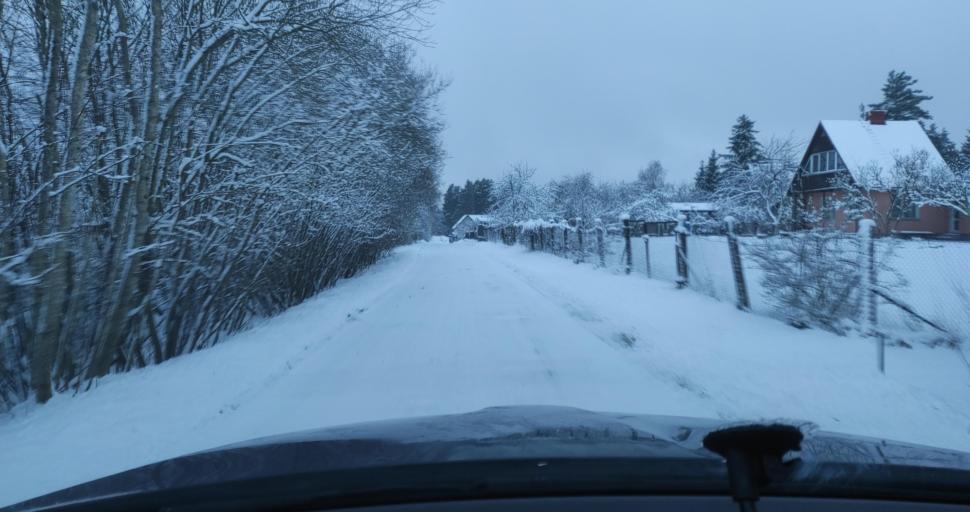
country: LV
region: Kuldigas Rajons
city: Kuldiga
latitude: 56.9919
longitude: 22.0429
